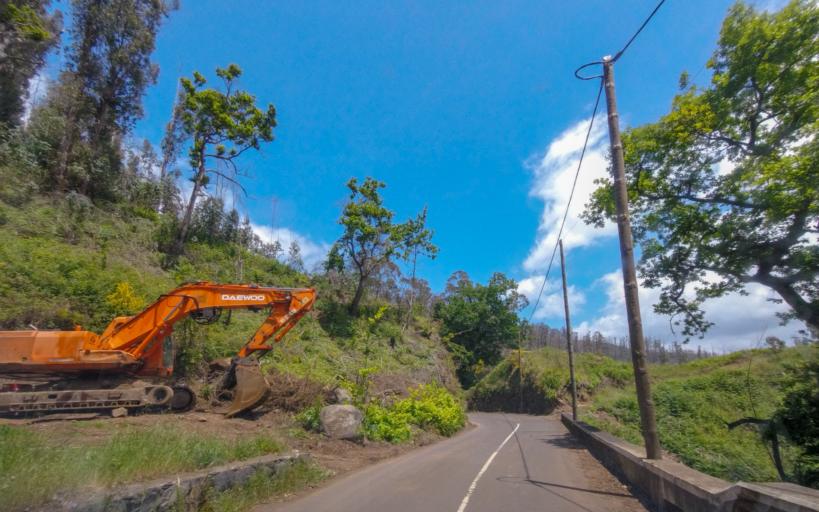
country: PT
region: Madeira
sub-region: Funchal
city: Nossa Senhora do Monte
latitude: 32.6821
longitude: -16.8871
